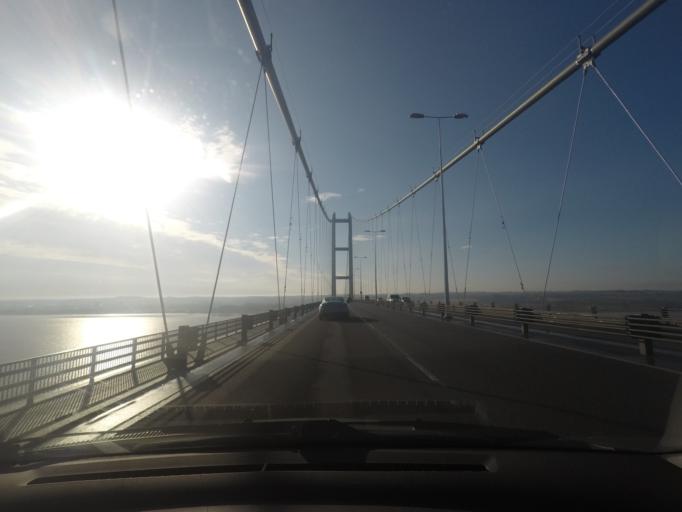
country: GB
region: England
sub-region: East Riding of Yorkshire
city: Hessle
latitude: 53.7061
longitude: -0.4497
